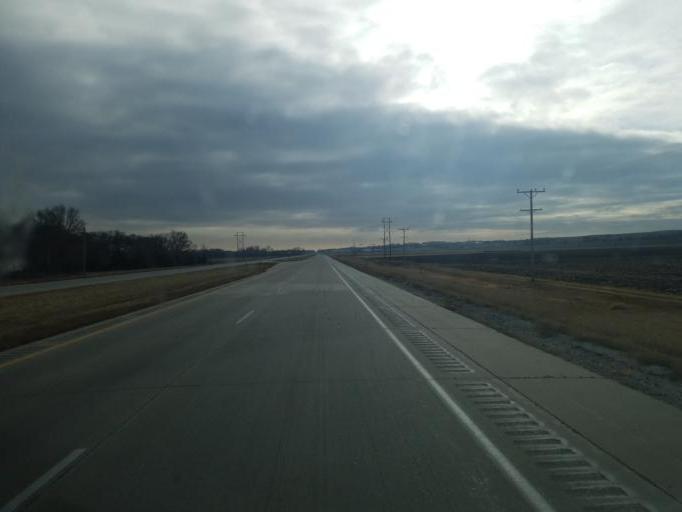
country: US
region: Nebraska
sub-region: Madison County
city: Norfolk
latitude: 42.0813
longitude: -97.4269
